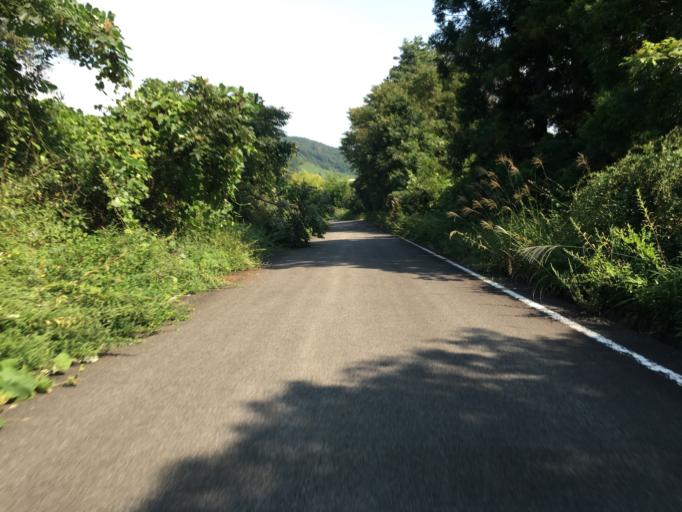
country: JP
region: Fukushima
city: Nihommatsu
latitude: 37.6095
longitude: 140.3885
